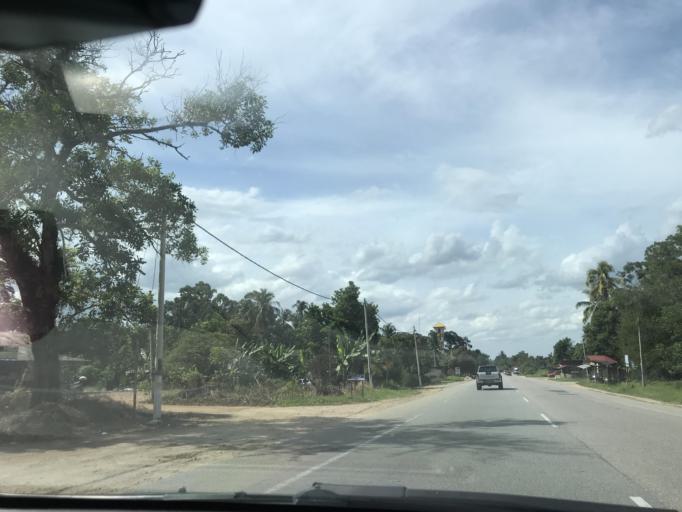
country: MY
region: Kelantan
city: Tanah Merah
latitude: 5.8415
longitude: 102.1601
